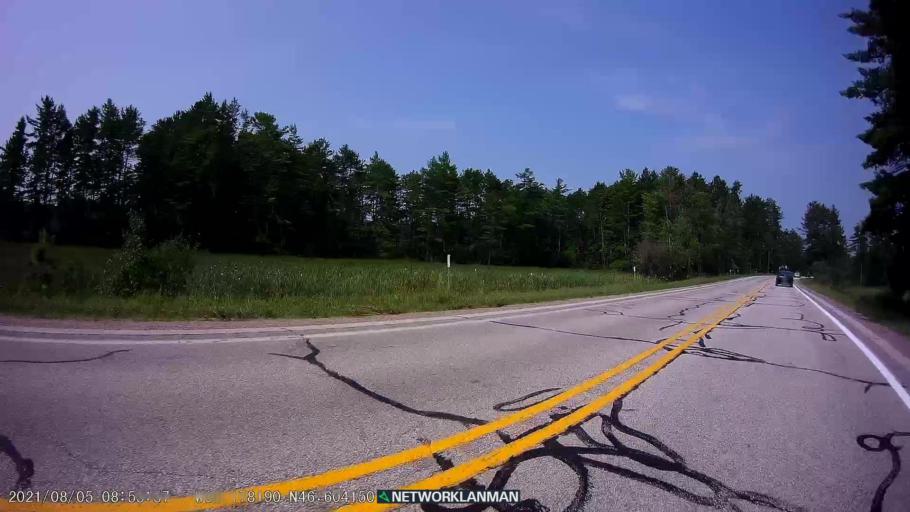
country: US
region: Michigan
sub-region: Luce County
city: Newberry
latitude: 46.6047
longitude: -85.1791
